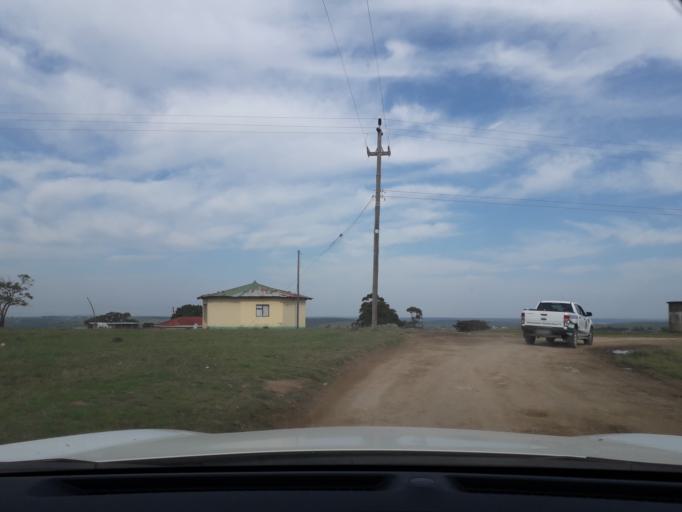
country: ZA
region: Eastern Cape
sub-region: Buffalo City Metropolitan Municipality
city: Bhisho
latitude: -32.9924
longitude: 27.3569
